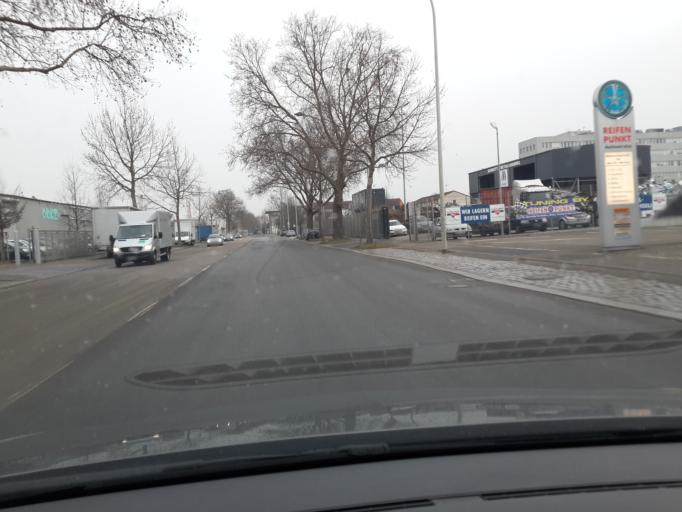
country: DE
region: Baden-Wuerttemberg
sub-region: Regierungsbezirk Stuttgart
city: Neckarsulm
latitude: 49.1744
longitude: 9.2180
